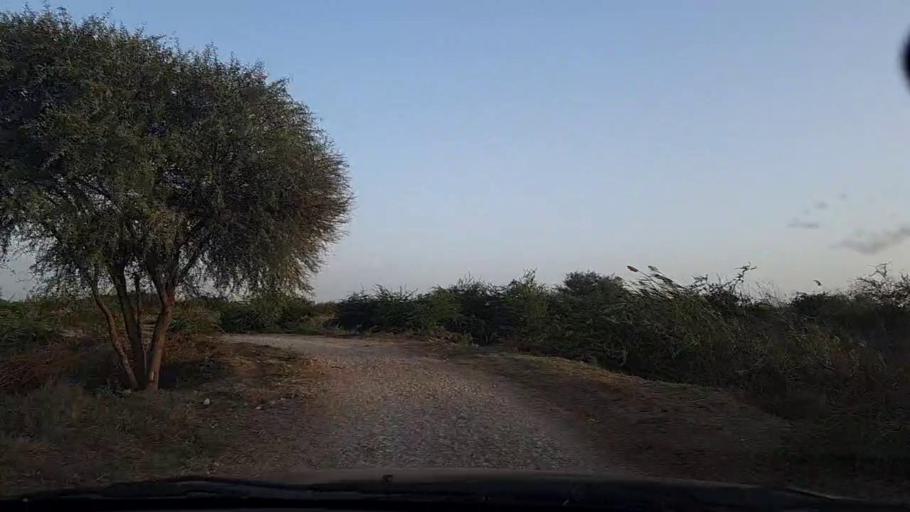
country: PK
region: Sindh
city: Keti Bandar
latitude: 24.1612
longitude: 67.5947
